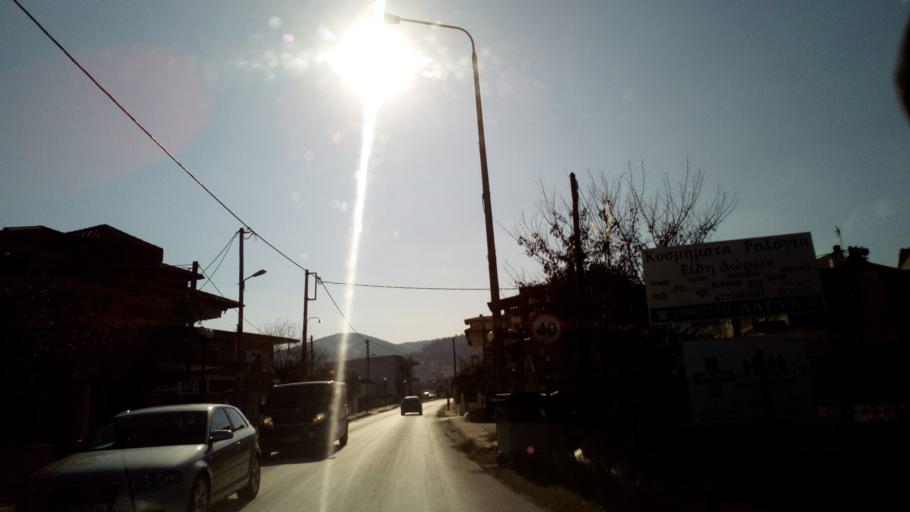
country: GR
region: Central Macedonia
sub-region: Nomos Thessalonikis
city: Lagyna
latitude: 40.7271
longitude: 23.0072
